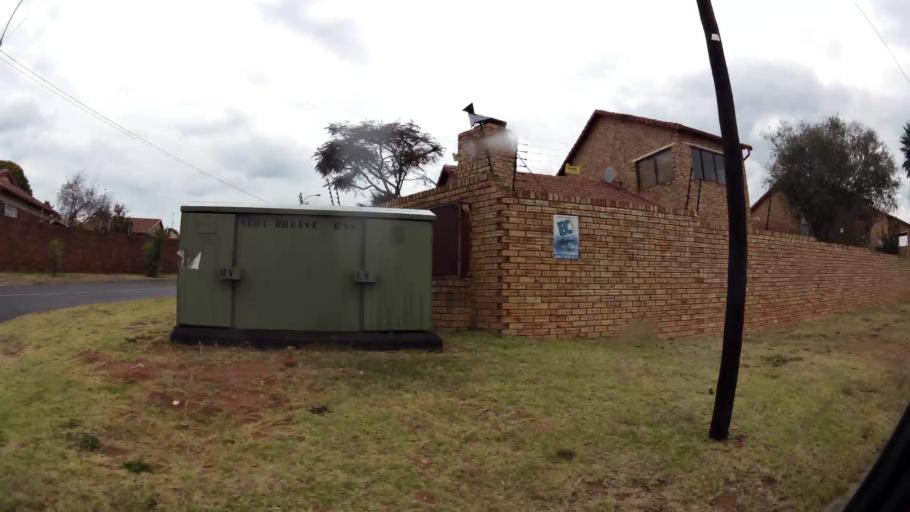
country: ZA
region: Gauteng
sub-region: City of Johannesburg Metropolitan Municipality
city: Roodepoort
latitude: -26.1067
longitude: 27.9173
